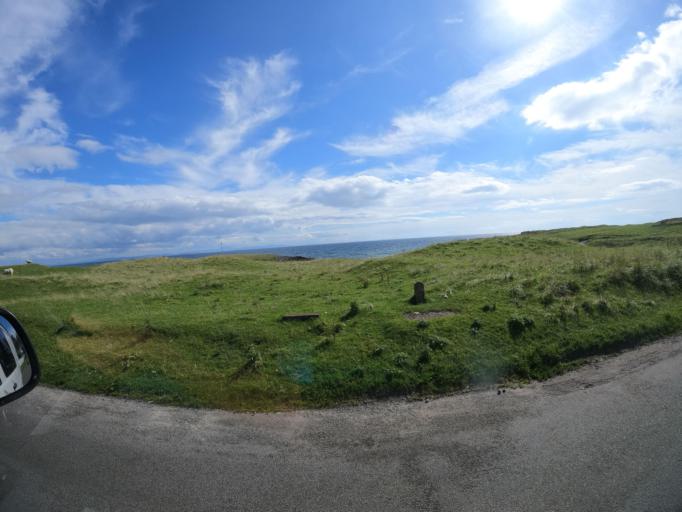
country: GB
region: Scotland
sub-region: Eilean Siar
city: Barra
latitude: 56.4984
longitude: -6.8101
